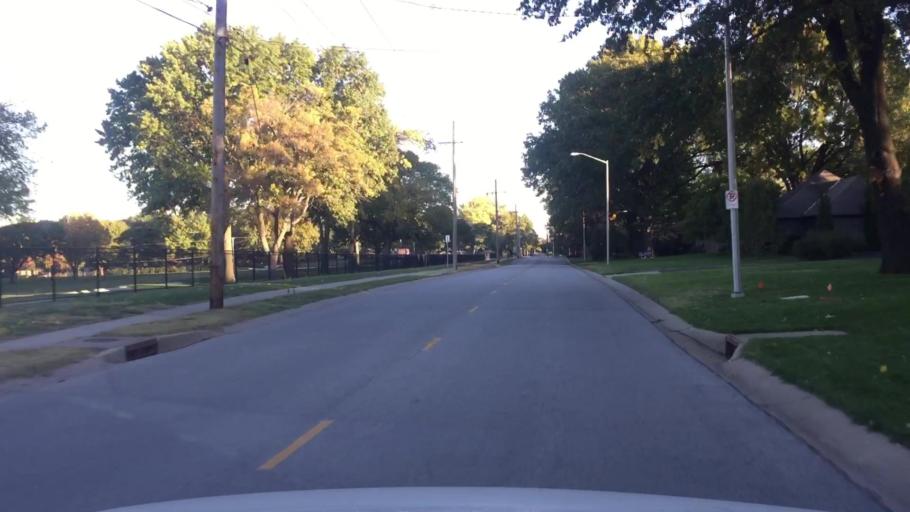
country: US
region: Kansas
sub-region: Johnson County
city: Overland Park
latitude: 39.0053
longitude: -94.6722
